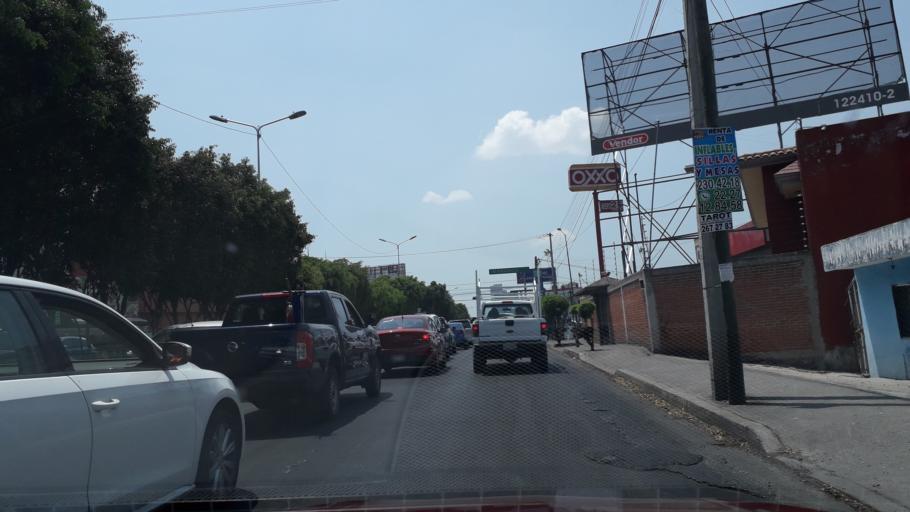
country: MX
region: Puebla
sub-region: San Pedro Cholula
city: Santiago Momoxpan
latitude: 19.0530
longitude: -98.2381
